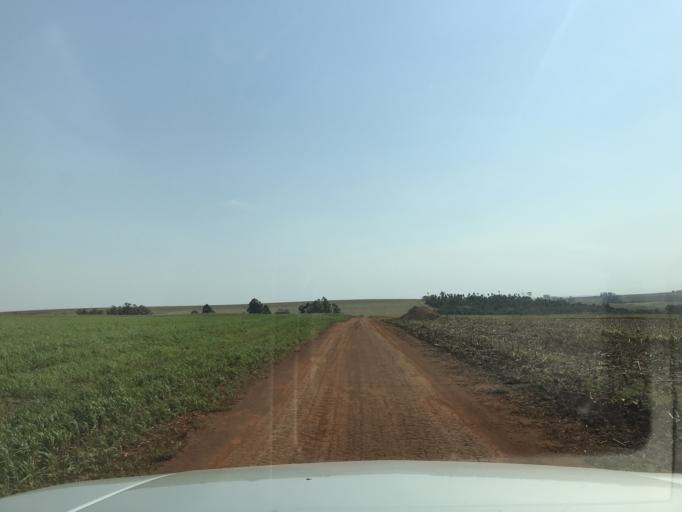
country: BR
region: Parana
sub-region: Palotina
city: Palotina
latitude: -24.2278
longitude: -53.7385
